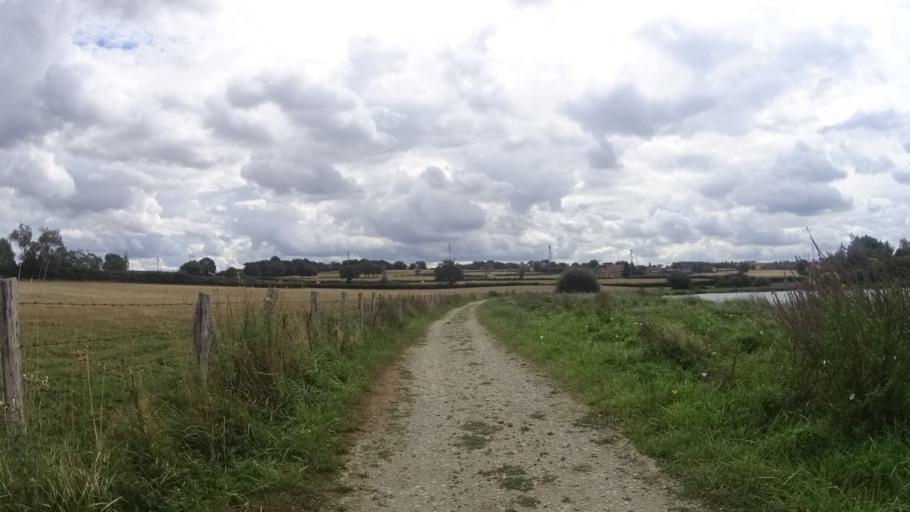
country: FR
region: Bourgogne
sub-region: Departement de Saone-et-Loire
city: Saint-Leu
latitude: 46.7393
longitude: 4.4882
